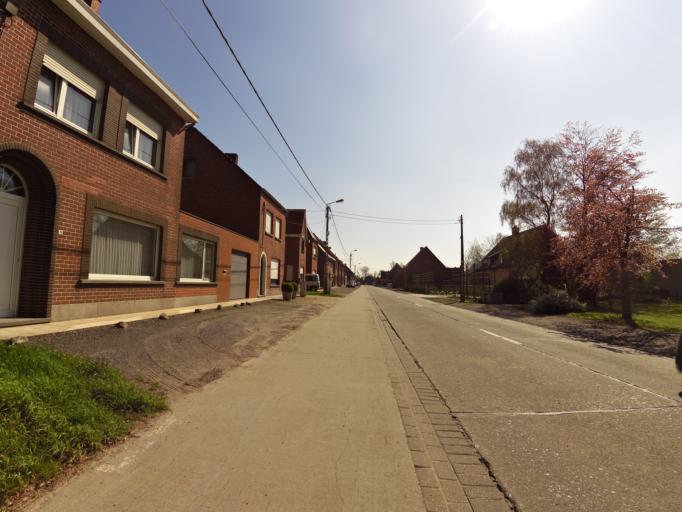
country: BE
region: Flanders
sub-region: Provincie West-Vlaanderen
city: Kortemark
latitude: 51.0416
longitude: 3.0353
